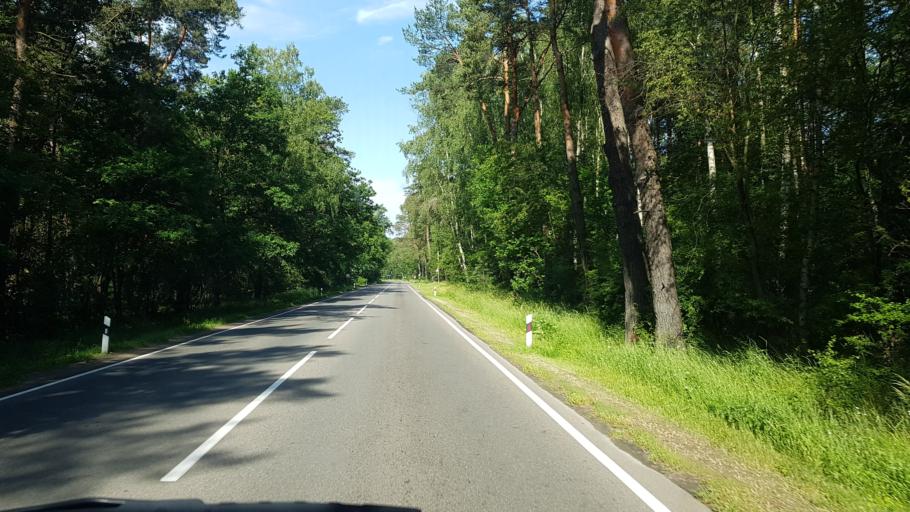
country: RU
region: Kaliningrad
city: Vzmorye
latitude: 54.7047
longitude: 20.2879
